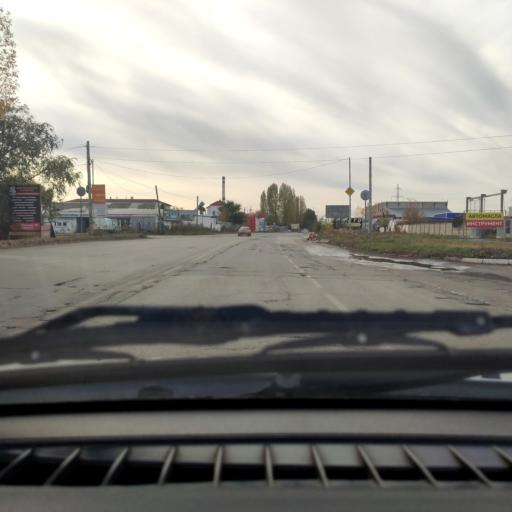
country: RU
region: Samara
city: Tol'yatti
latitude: 53.5228
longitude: 49.4699
